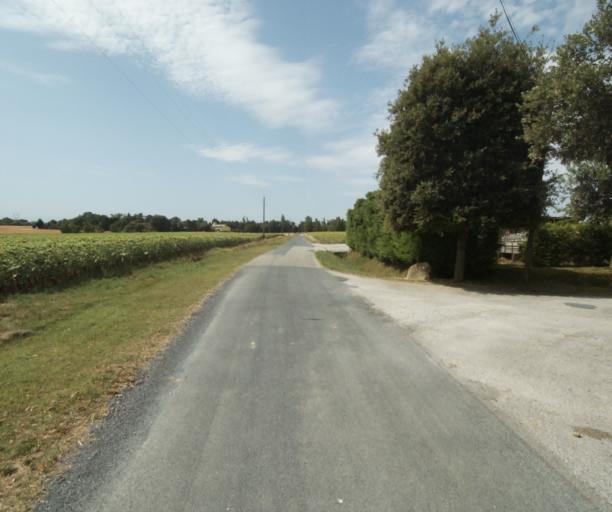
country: FR
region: Midi-Pyrenees
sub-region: Departement de la Haute-Garonne
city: Saint-Felix-Lauragais
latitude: 43.4309
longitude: 1.9019
